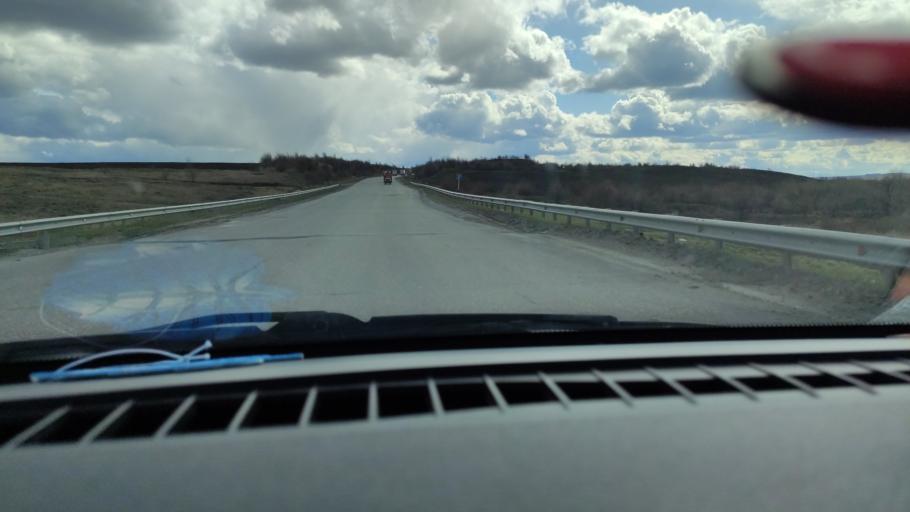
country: RU
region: Samara
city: Varlamovo
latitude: 53.0672
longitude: 48.3537
